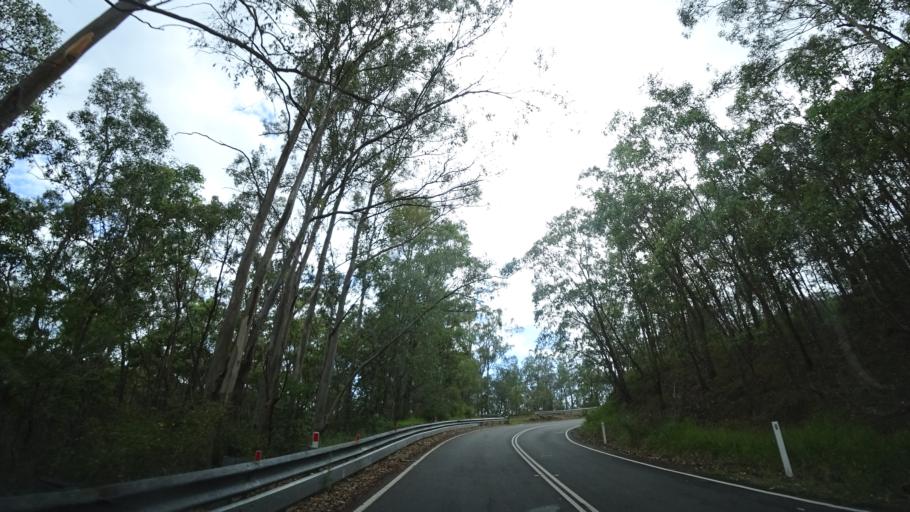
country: AU
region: Queensland
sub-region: Brisbane
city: Taringa
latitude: -27.4632
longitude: 152.9570
